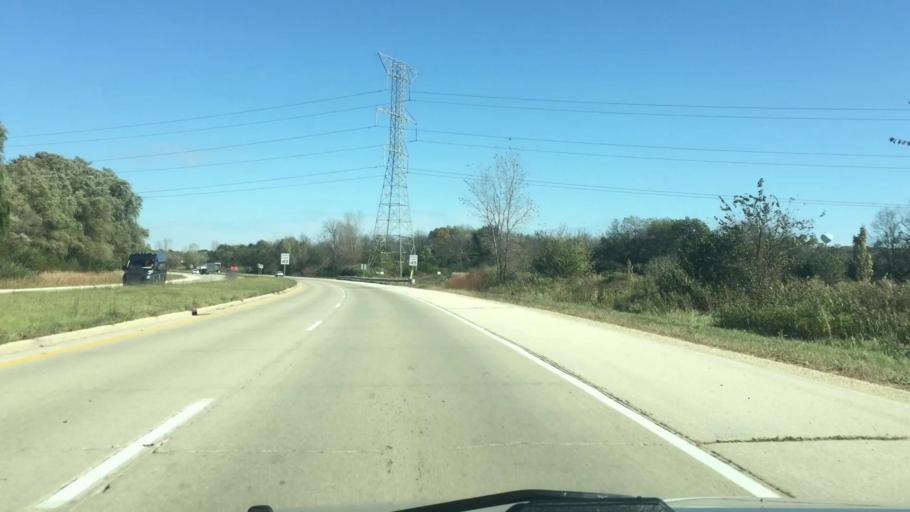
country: US
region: Wisconsin
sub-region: Waukesha County
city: Waukesha
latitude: 42.9804
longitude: -88.2146
